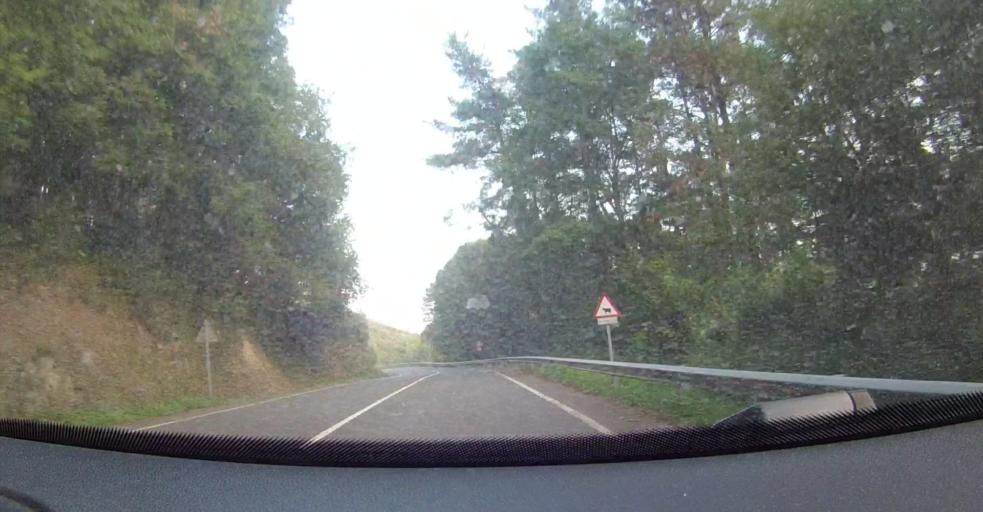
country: ES
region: Basque Country
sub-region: Bizkaia
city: Sopuerta
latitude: 43.2984
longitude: -3.1684
